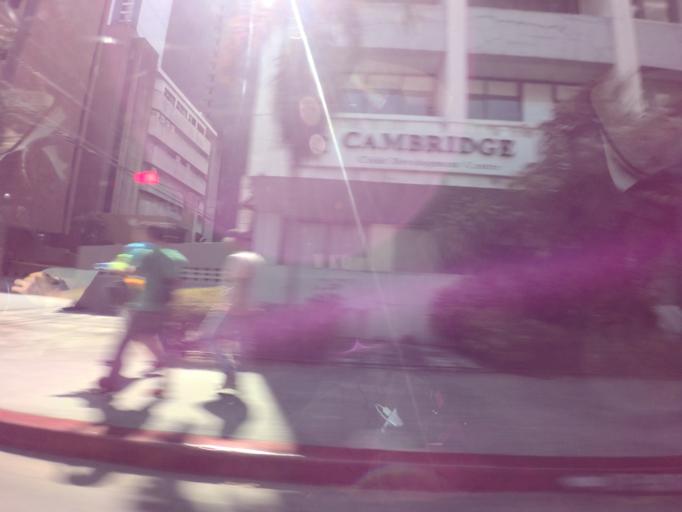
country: PH
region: Metro Manila
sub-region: Makati City
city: Makati City
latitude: 14.5604
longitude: 121.0208
